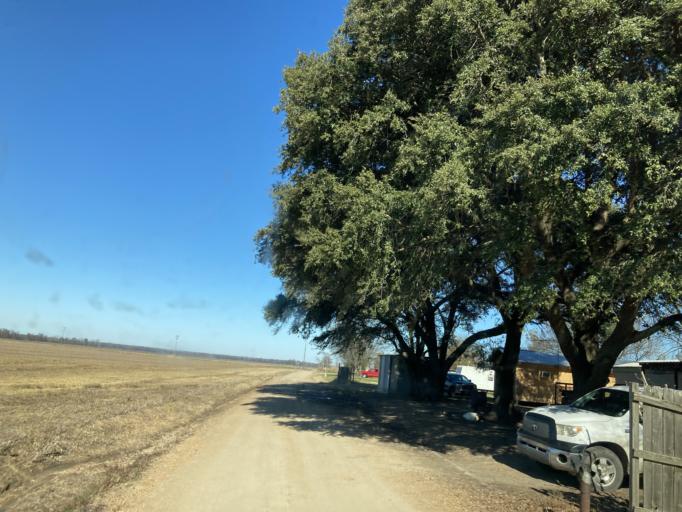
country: US
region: Mississippi
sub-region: Sharkey County
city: Rolling Fork
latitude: 32.8192
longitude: -90.7113
